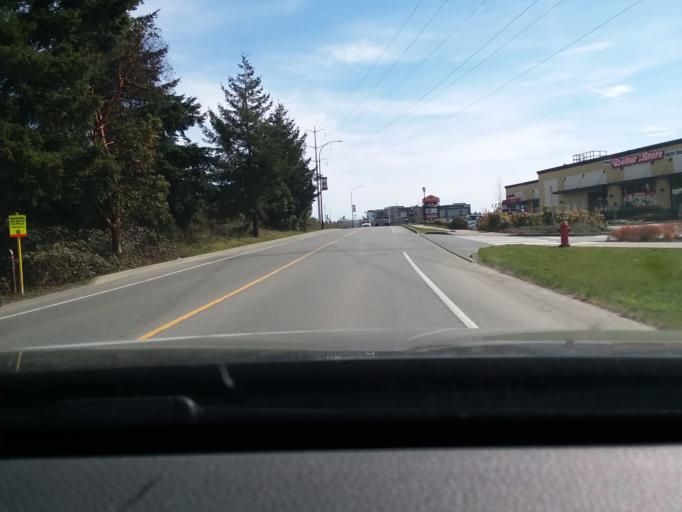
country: CA
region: British Columbia
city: Langford
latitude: 48.4433
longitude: -123.5163
